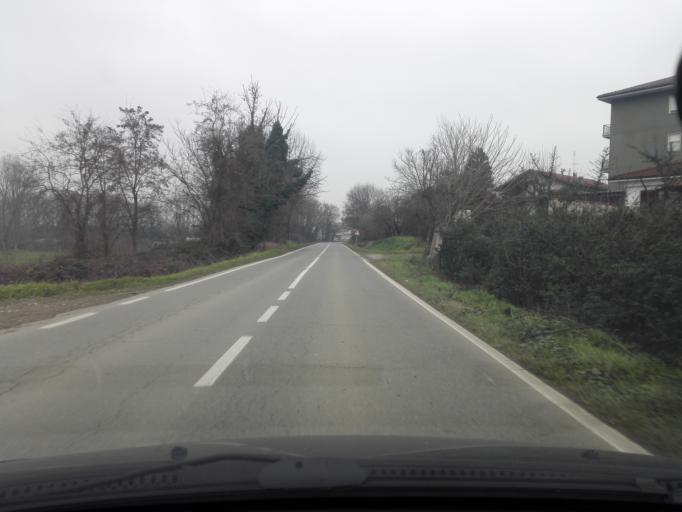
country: IT
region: Piedmont
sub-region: Provincia di Alessandria
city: Bosco Marengo
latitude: 44.8255
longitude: 8.6752
